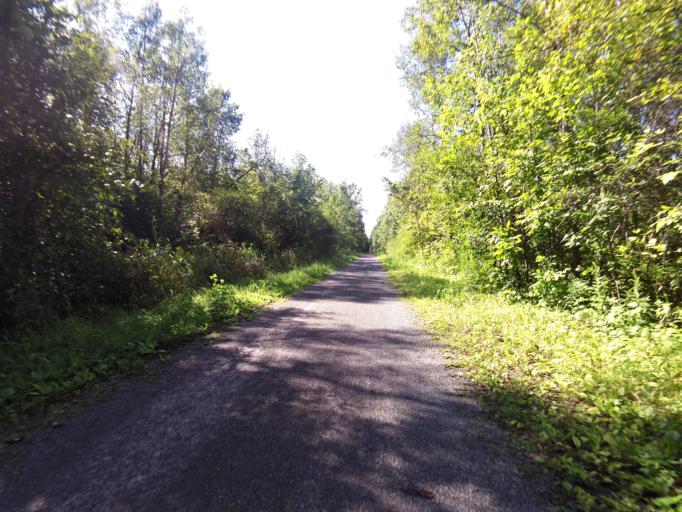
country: CA
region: Ontario
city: Ottawa
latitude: 45.1841
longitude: -75.6200
